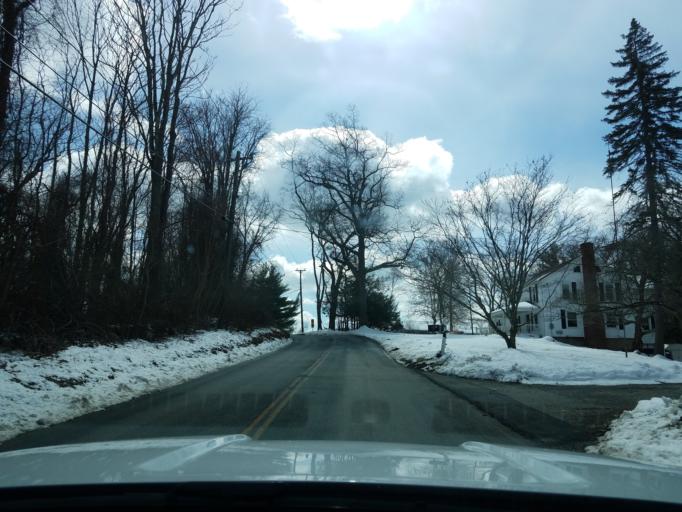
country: US
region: Connecticut
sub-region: Litchfield County
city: New Milford
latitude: 41.5583
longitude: -73.3943
